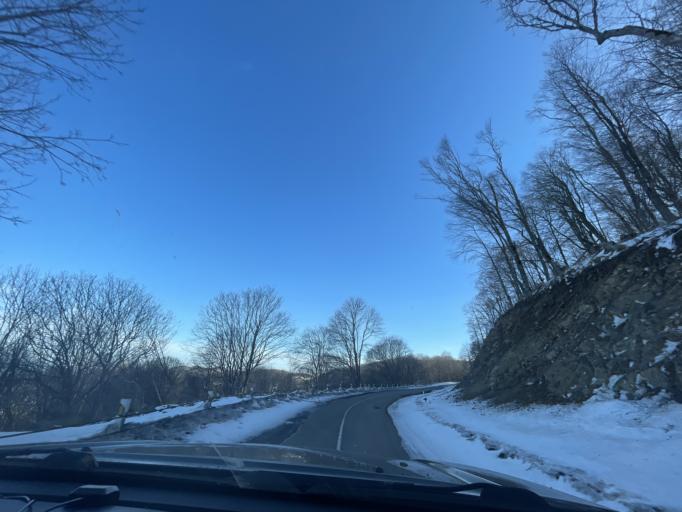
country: GE
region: Kvemo Kartli
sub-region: Tetri Tsqaro
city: Manglisi
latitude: 41.7702
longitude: 44.5070
